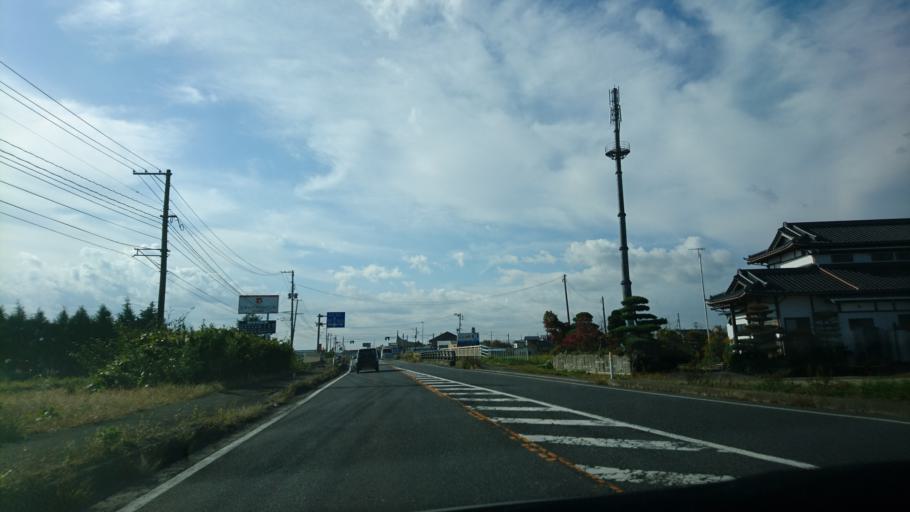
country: JP
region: Miyagi
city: Furukawa
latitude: 38.6173
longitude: 140.9840
